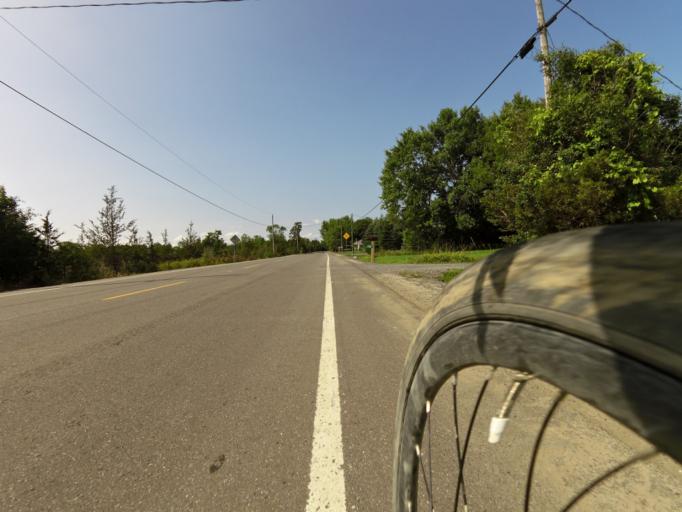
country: CA
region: Ontario
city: Skatepark
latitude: 44.2514
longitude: -76.7217
